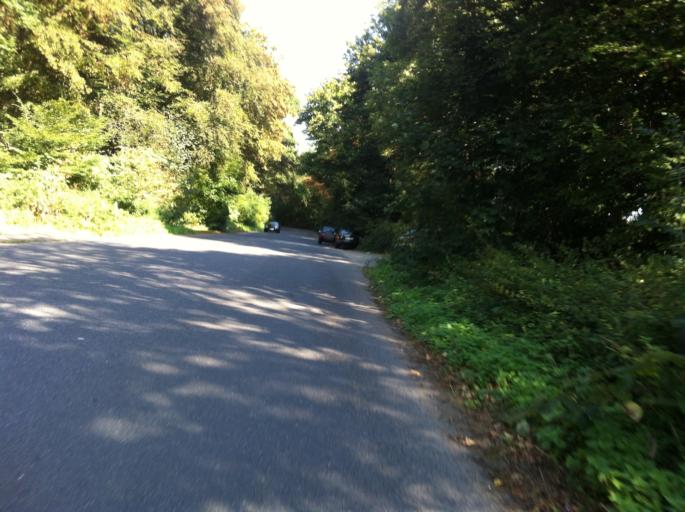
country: DE
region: North Rhine-Westphalia
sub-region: Regierungsbezirk Koln
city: Hoehenberg
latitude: 50.9166
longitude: 7.0225
